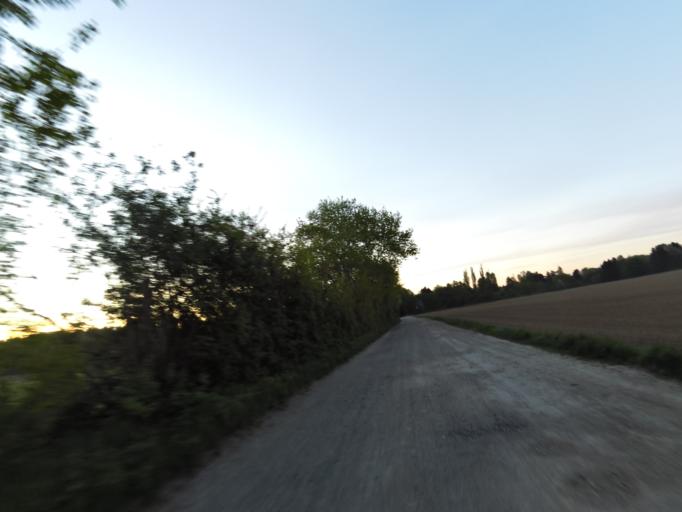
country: DE
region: North Rhine-Westphalia
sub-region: Regierungsbezirk Koln
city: Wachtberg
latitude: 50.6814
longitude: 7.0624
